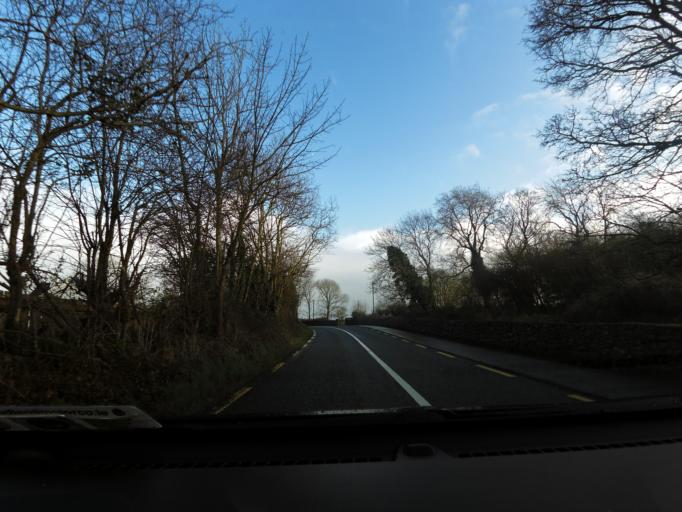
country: IE
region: Connaught
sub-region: County Galway
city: Tuam
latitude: 53.4897
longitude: -8.9293
